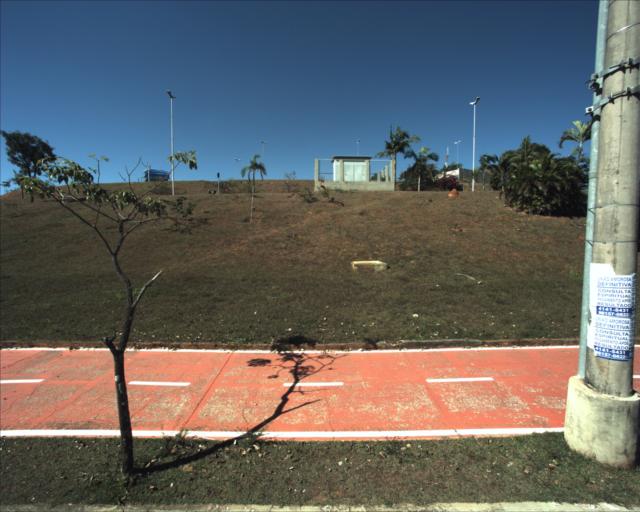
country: BR
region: Sao Paulo
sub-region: Sorocaba
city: Sorocaba
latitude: -23.4752
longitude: -47.4250
